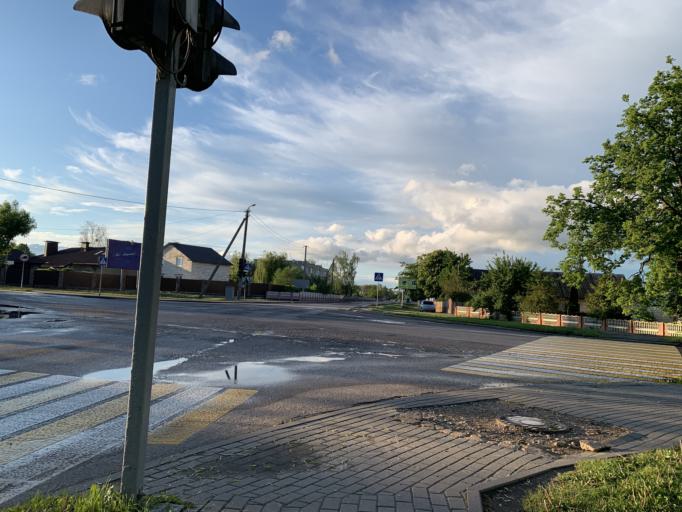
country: BY
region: Minsk
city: Nyasvizh
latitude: 53.2126
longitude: 26.6980
